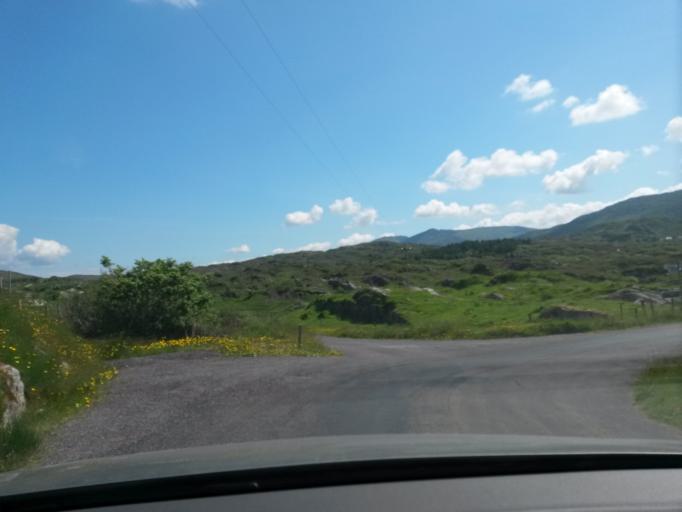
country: IE
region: Munster
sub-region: Ciarrai
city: Cahersiveen
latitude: 51.7180
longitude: -9.9557
